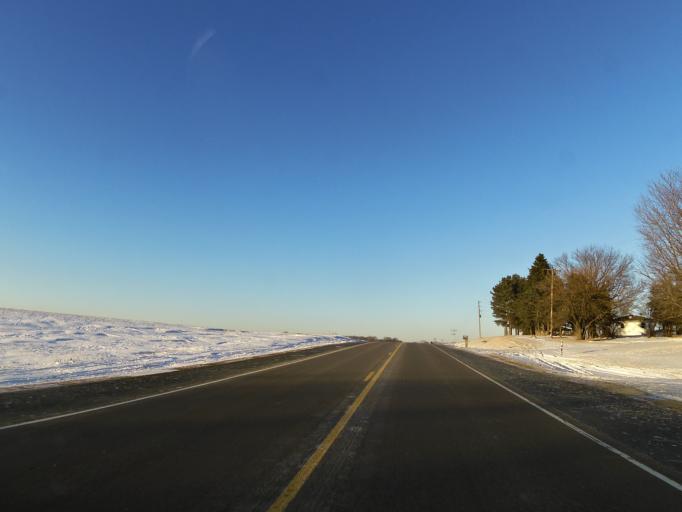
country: US
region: Minnesota
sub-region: Dakota County
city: Farmington
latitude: 44.5712
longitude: -93.1368
